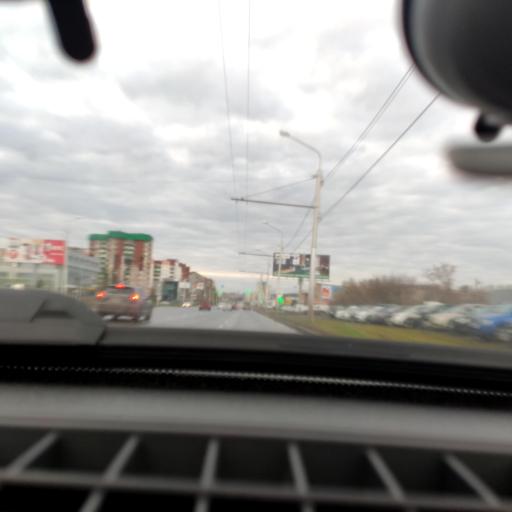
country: RU
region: Bashkortostan
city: Ufa
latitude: 54.7819
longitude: 56.0728
